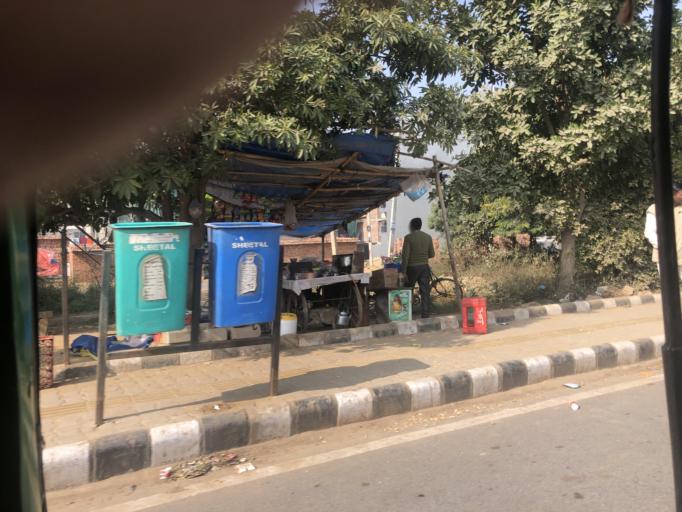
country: IN
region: Haryana
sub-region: Gurgaon
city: Gurgaon
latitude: 28.4270
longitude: 77.0911
